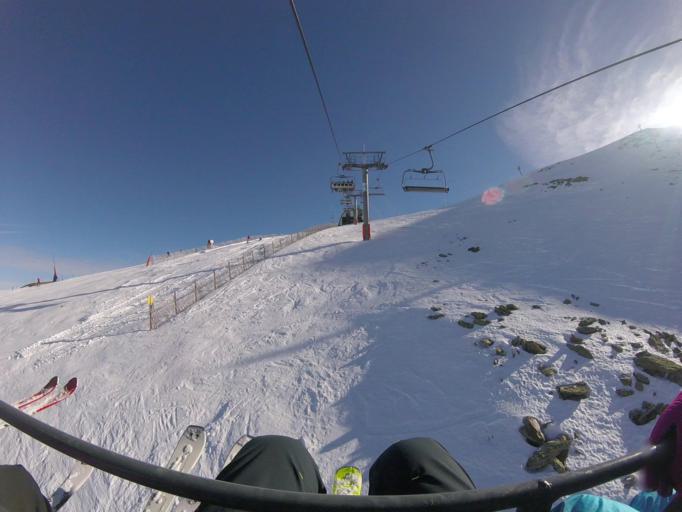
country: AD
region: Encamp
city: Pas de la Casa
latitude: 42.5259
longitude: 1.7221
